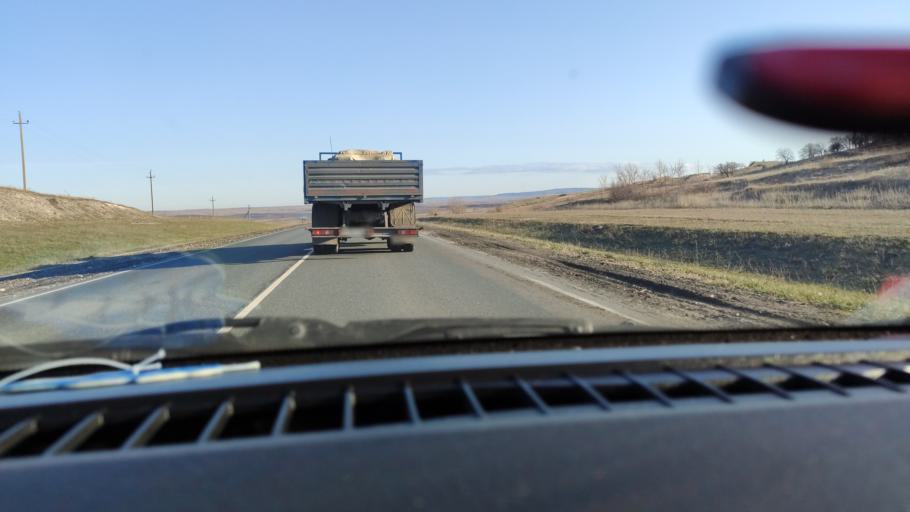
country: RU
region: Saratov
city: Alekseyevka
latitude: 52.3236
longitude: 47.9213
